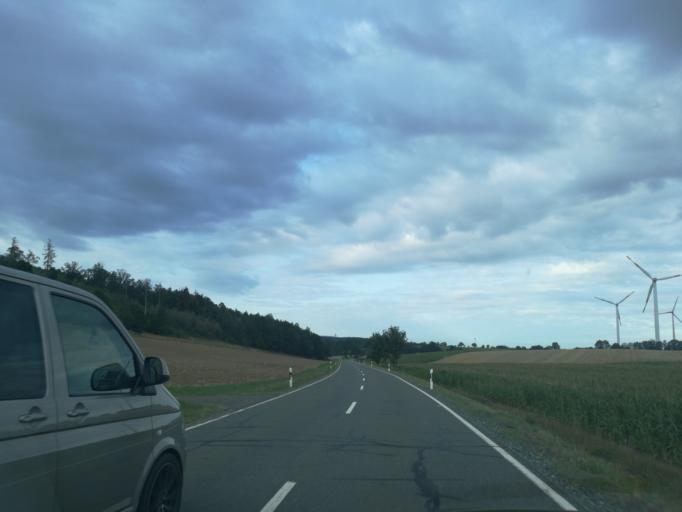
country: DE
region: Bavaria
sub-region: Upper Franconia
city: Gattendorf
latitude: 50.3019
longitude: 12.0149
